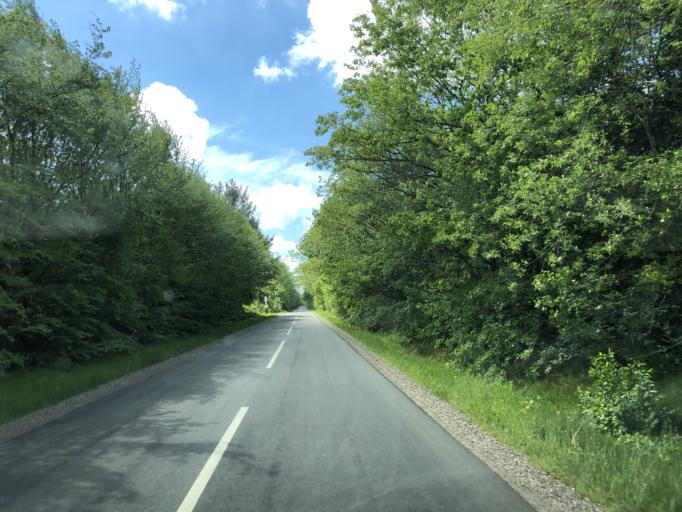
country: DK
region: Central Jutland
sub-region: Ringkobing-Skjern Kommune
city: Tarm
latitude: 55.9409
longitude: 8.5654
